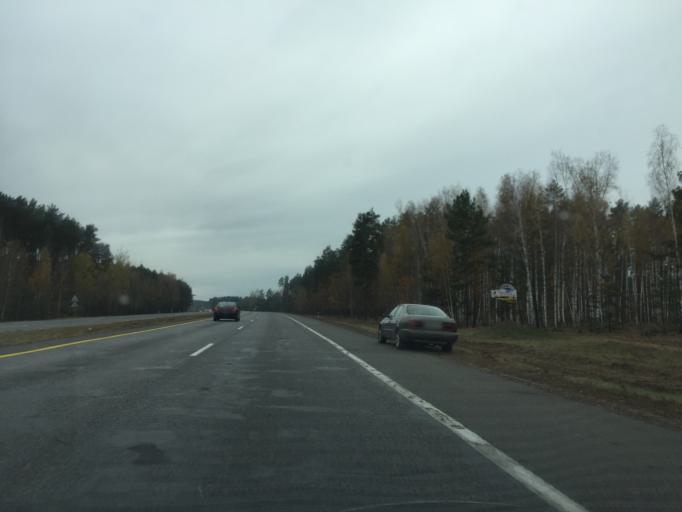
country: BY
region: Gomel
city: Horad Rechytsa
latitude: 52.3605
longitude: 30.6480
